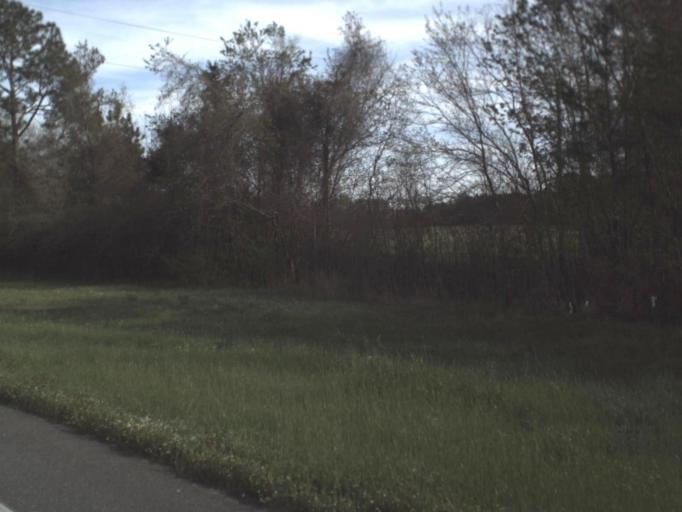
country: US
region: Florida
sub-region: Holmes County
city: Bonifay
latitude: 30.7859
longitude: -85.6542
